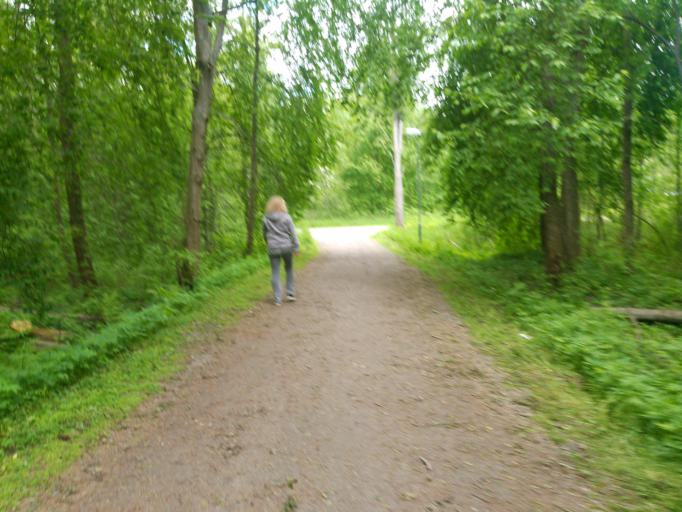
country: SE
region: Vaesterbotten
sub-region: Umea Kommun
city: Umea
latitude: 63.8241
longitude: 20.2389
